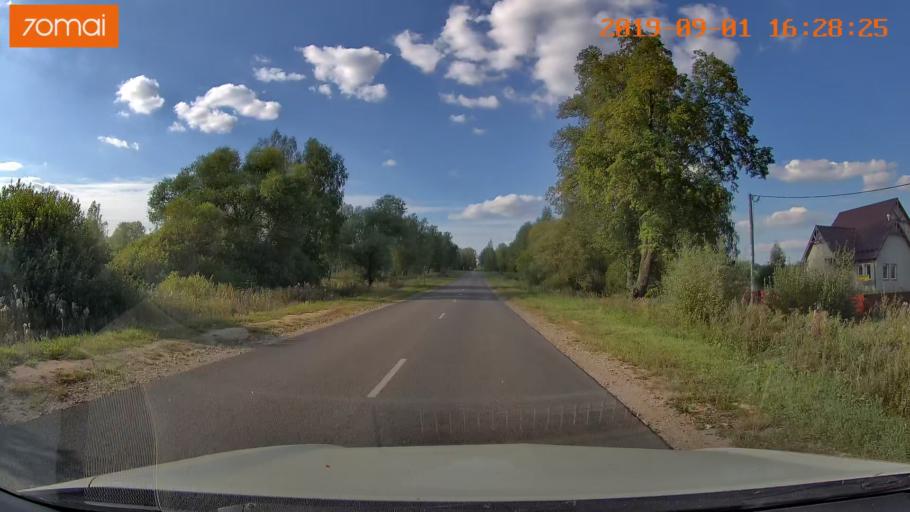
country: RU
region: Kaluga
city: Maloyaroslavets
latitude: 54.9259
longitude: 36.4742
